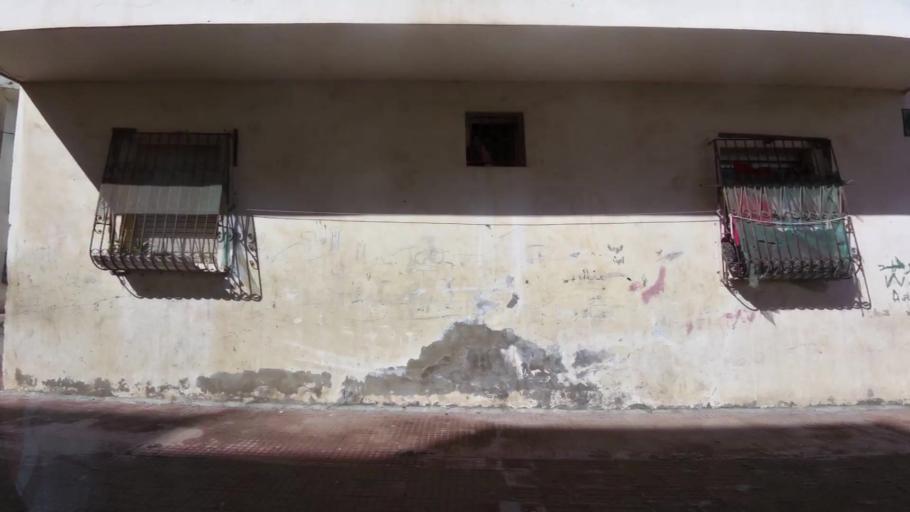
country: MA
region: Chaouia-Ouardigha
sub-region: Settat Province
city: Berrechid
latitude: 33.2586
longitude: -7.5666
